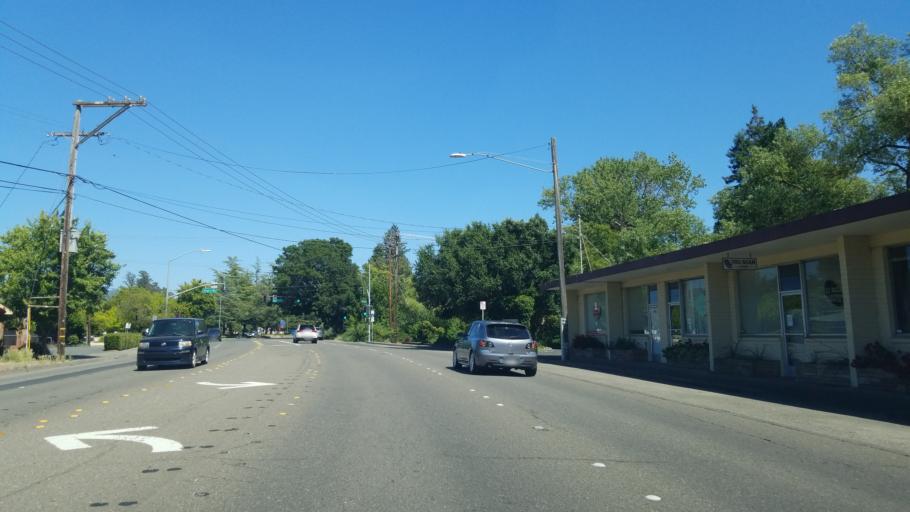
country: US
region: California
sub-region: Sonoma County
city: Santa Rosa
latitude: 38.4503
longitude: -122.6937
